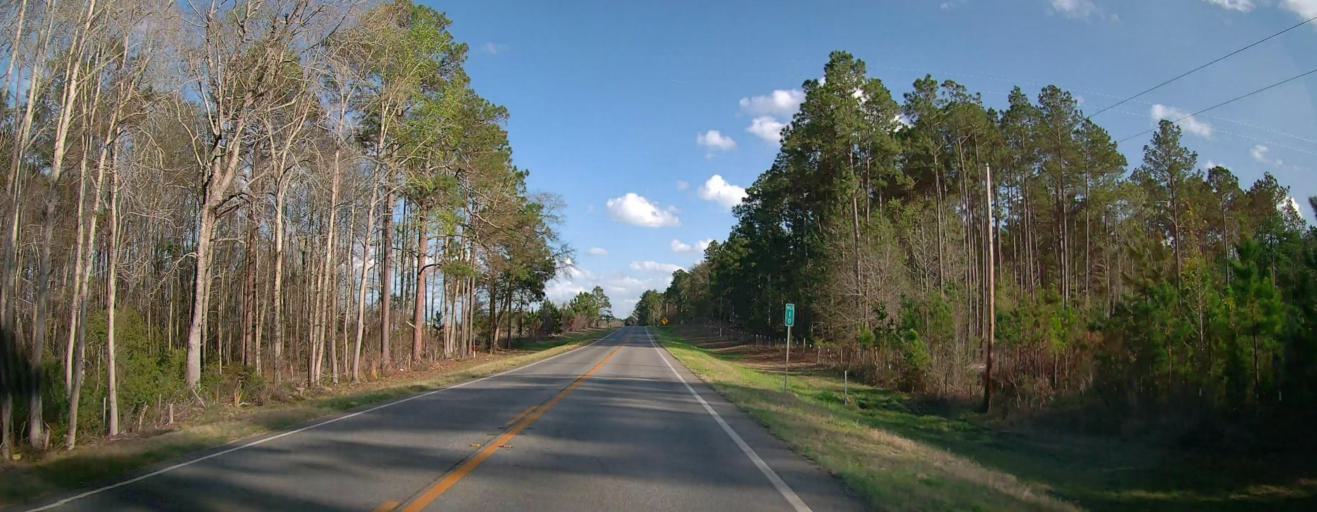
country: US
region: Georgia
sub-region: Toombs County
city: Lyons
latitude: 32.1782
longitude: -82.2880
